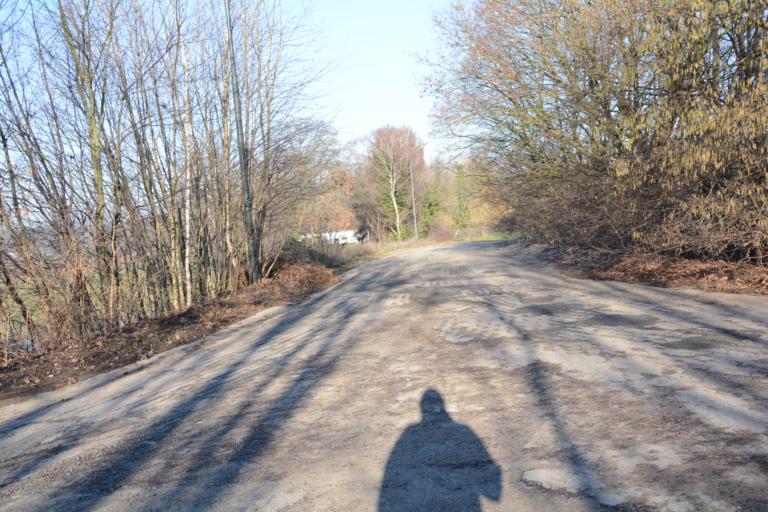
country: BE
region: Flanders
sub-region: Provincie Vlaams-Brabant
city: Bever
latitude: 50.9111
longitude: 4.3335
